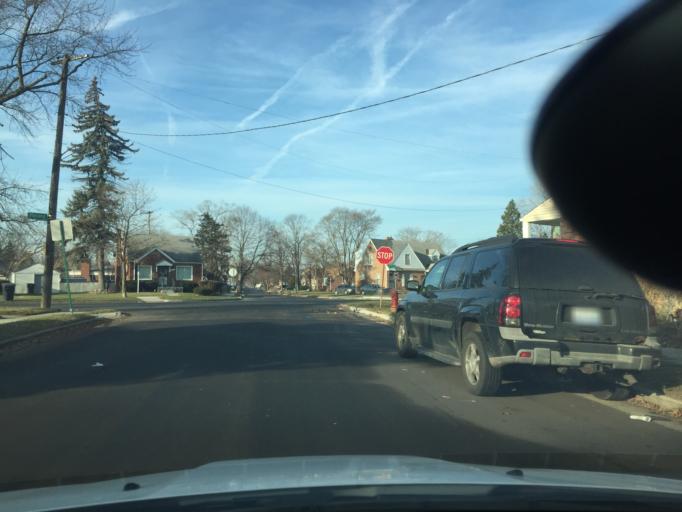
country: US
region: Michigan
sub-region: Macomb County
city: Eastpointe
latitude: 42.4347
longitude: -82.9610
